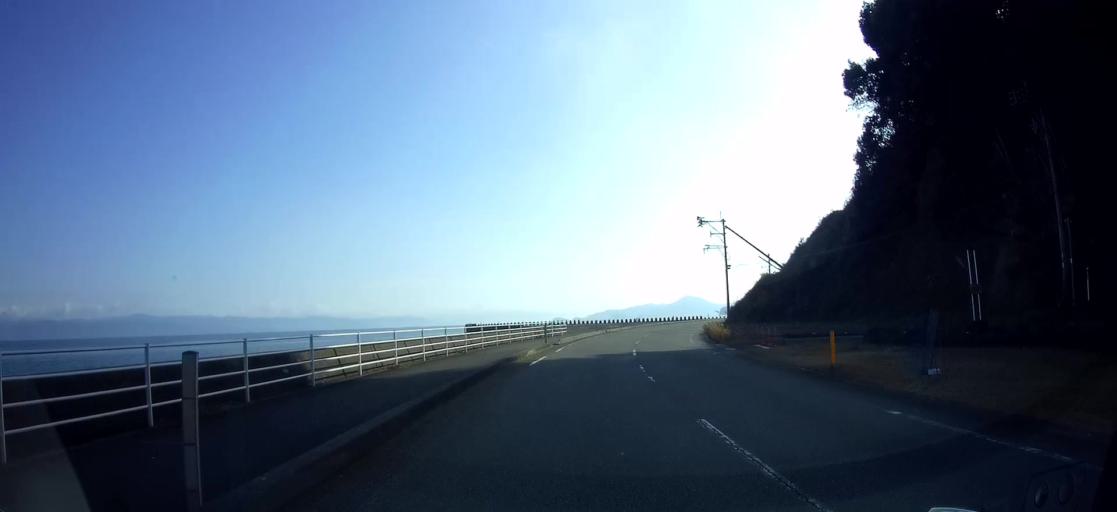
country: JP
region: Kumamoto
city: Yatsushiro
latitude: 32.4563
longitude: 130.4287
